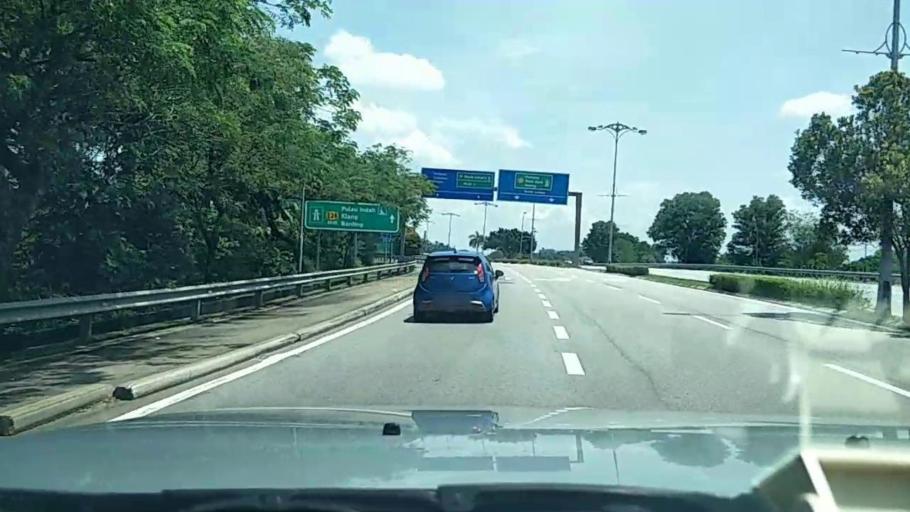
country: MY
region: Putrajaya
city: Putrajaya
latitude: 2.9450
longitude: 101.6674
